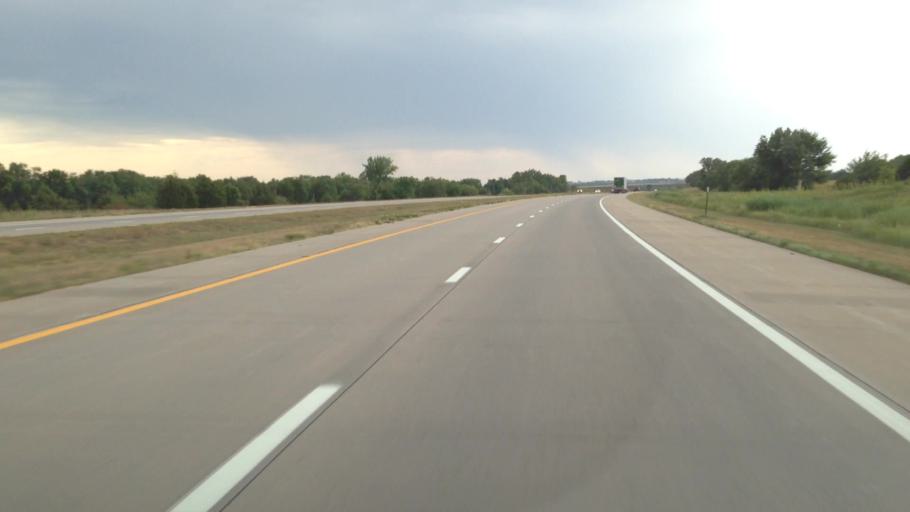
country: US
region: Kansas
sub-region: Osage County
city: Lyndon
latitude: 38.4584
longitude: -95.5544
